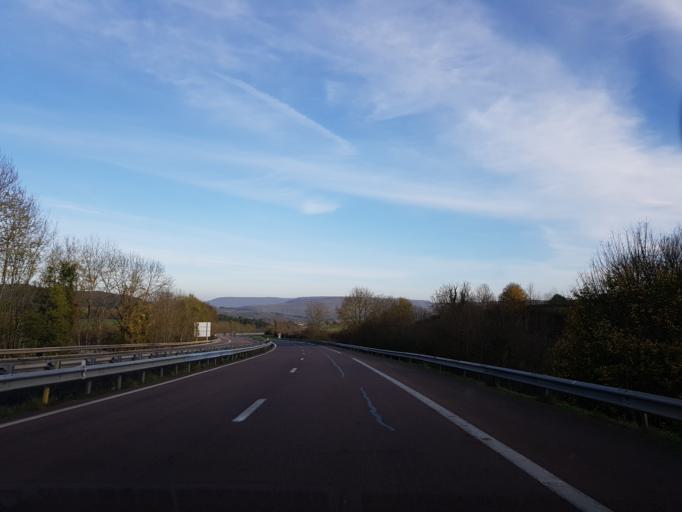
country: FR
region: Bourgogne
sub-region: Departement de la Cote-d'Or
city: Fleurey-sur-Ouche
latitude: 47.3054
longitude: 4.7494
